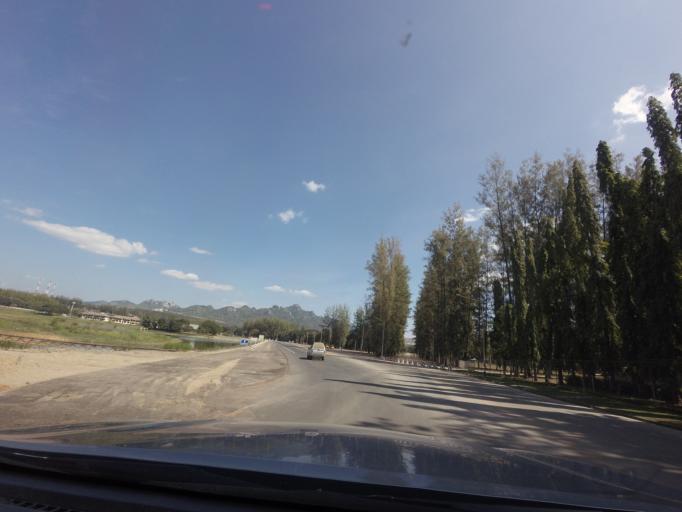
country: TH
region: Lampang
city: Mae Mo
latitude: 18.3042
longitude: 99.7348
